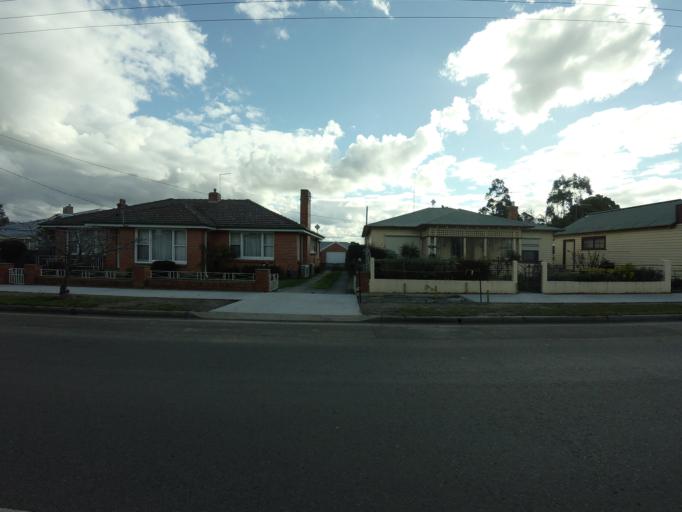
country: AU
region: Tasmania
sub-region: Northern Midlands
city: Longford
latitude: -41.6868
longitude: 147.0801
